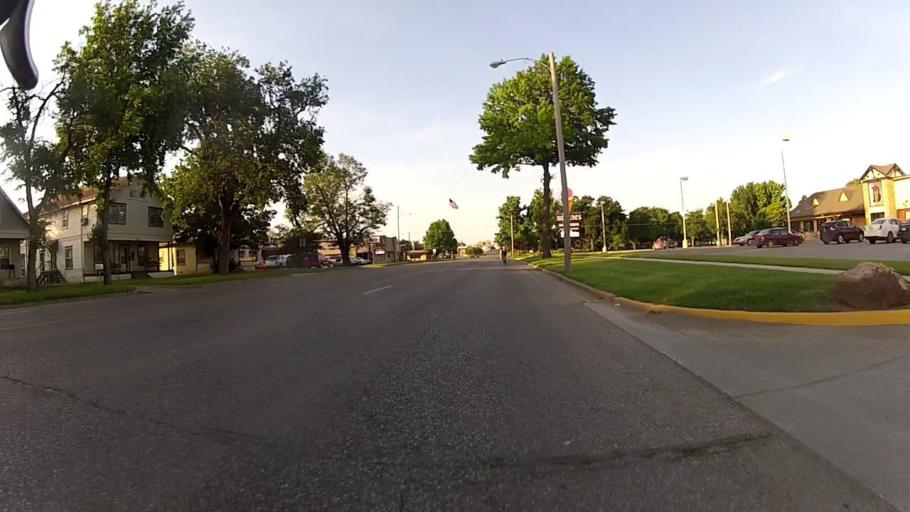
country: US
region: Kansas
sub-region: Cowley County
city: Arkansas City
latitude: 37.0715
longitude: -97.0392
